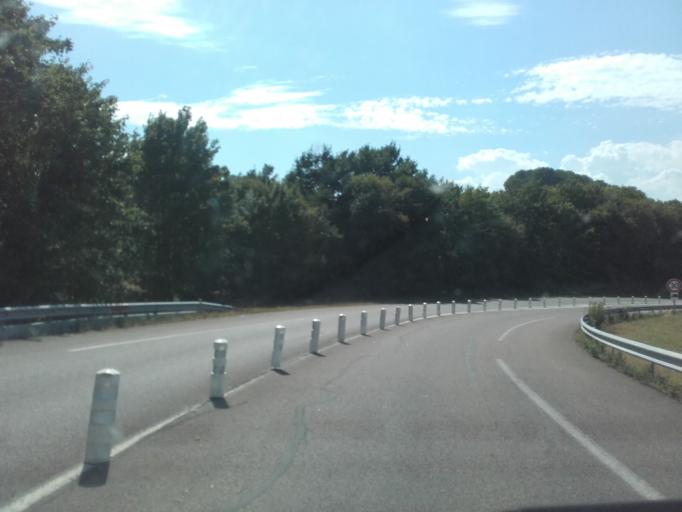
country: FR
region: Bourgogne
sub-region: Departement de la Cote-d'Or
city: Pouilly-en-Auxois
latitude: 47.2514
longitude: 4.5555
